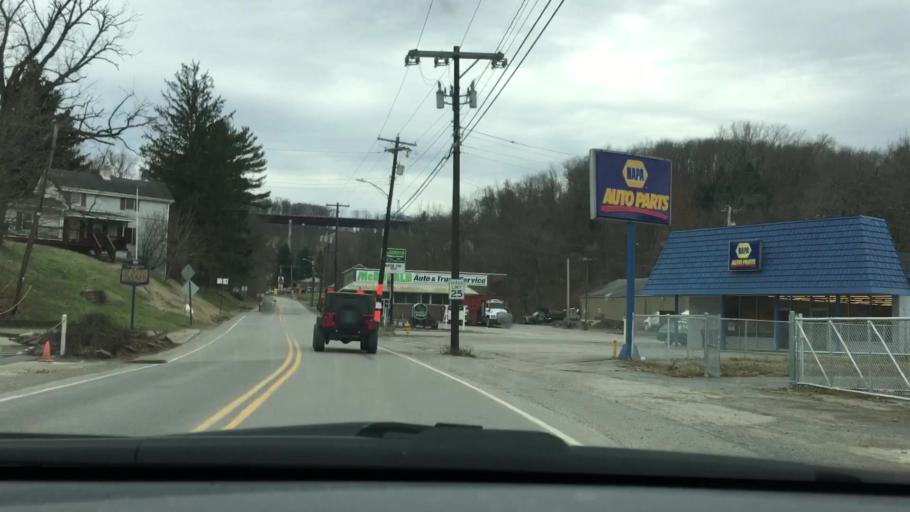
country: US
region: Pennsylvania
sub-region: Washington County
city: McDonald
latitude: 40.3670
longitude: -80.2350
